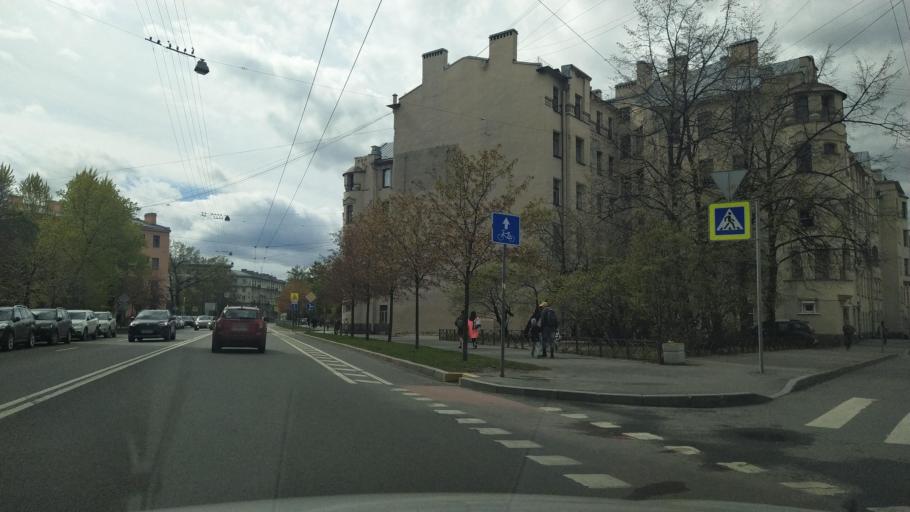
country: RU
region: St.-Petersburg
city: Petrogradka
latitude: 59.9668
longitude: 30.3028
